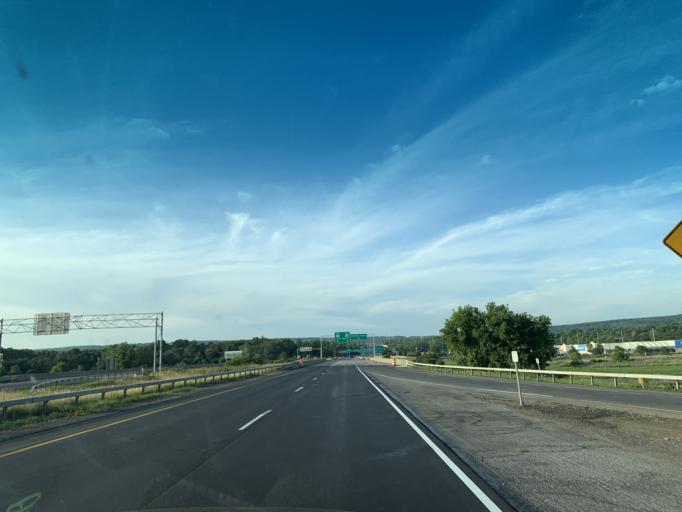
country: US
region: New York
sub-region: Oneida County
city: Utica
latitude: 43.1208
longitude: -75.2312
